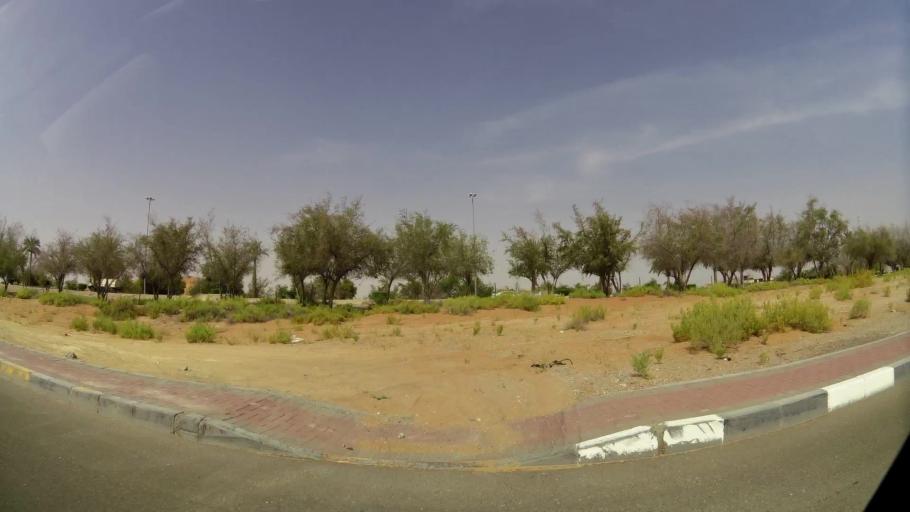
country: AE
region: Abu Dhabi
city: Al Ain
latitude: 24.1536
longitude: 55.6762
